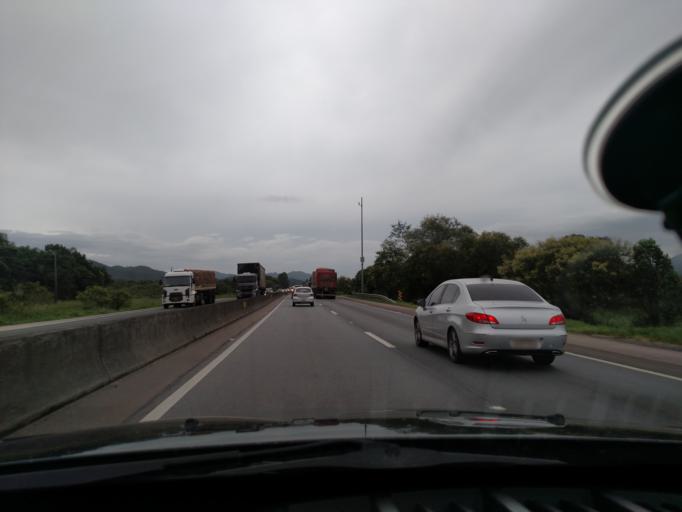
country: BR
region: Santa Catarina
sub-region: Biguacu
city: Biguacu
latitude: -27.4213
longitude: -48.6254
